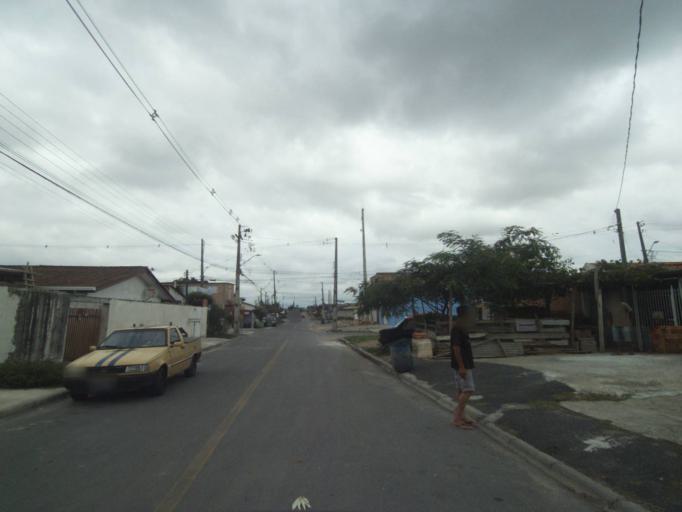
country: BR
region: Parana
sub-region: Pinhais
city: Pinhais
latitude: -25.4479
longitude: -49.1995
